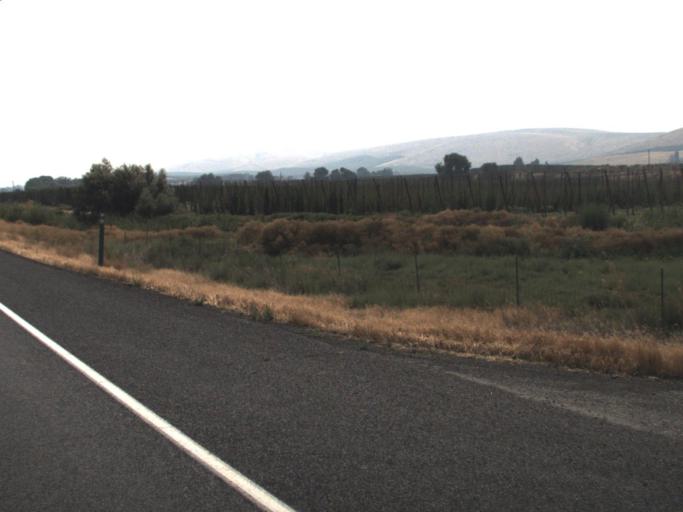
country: US
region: Washington
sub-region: Yakima County
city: Terrace Heights
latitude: 46.5442
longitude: -120.3210
